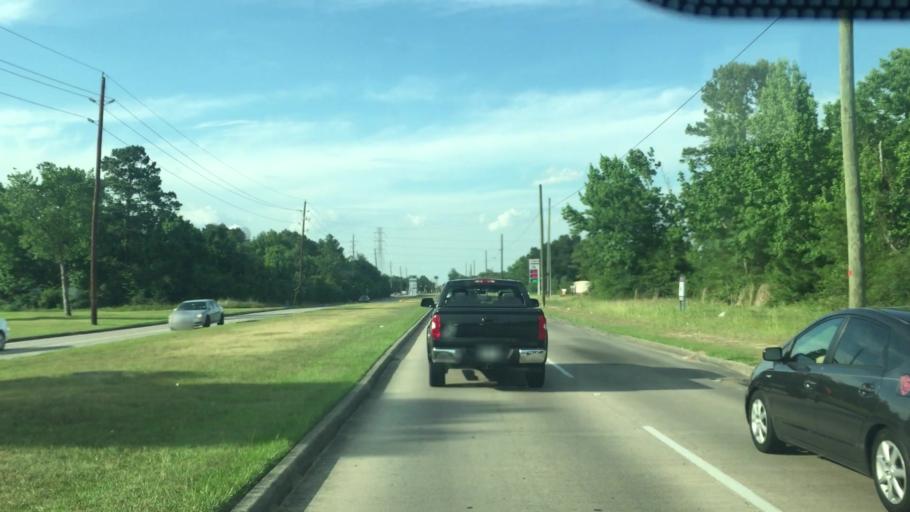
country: US
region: Texas
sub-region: Harris County
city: Hudson
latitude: 29.9681
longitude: -95.4962
